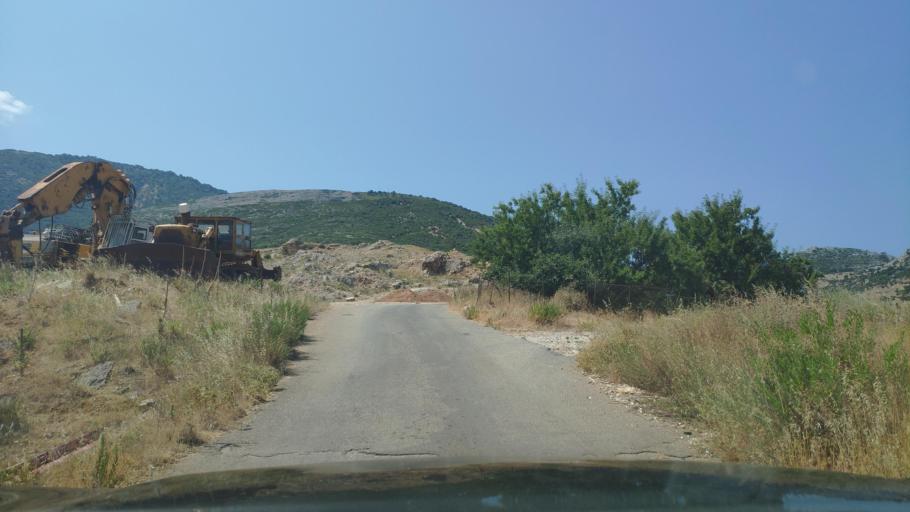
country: GR
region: West Greece
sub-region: Nomos Aitolias kai Akarnanias
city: Monastirakion
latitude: 38.8467
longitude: 20.9443
